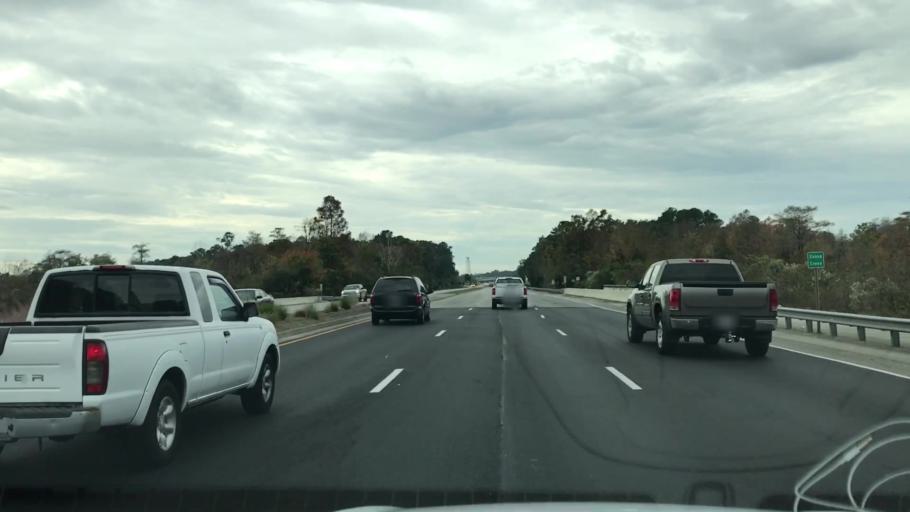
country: US
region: South Carolina
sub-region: Berkeley County
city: Goose Creek
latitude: 32.9852
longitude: -80.0416
